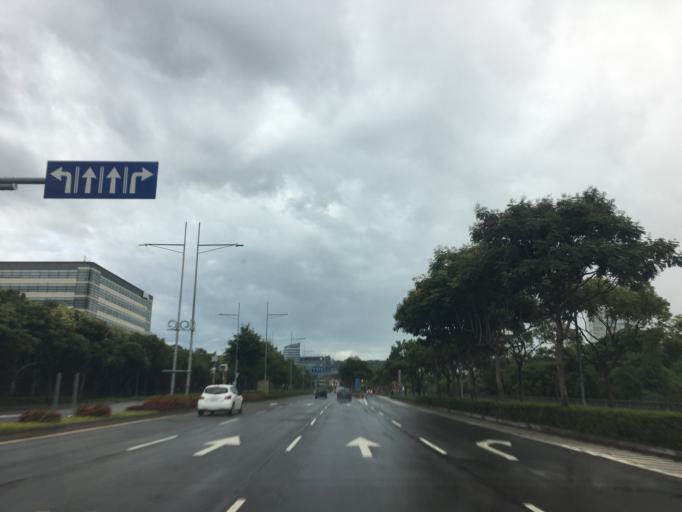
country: TW
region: Taiwan
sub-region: Taichung City
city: Taichung
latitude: 24.2074
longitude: 120.6225
